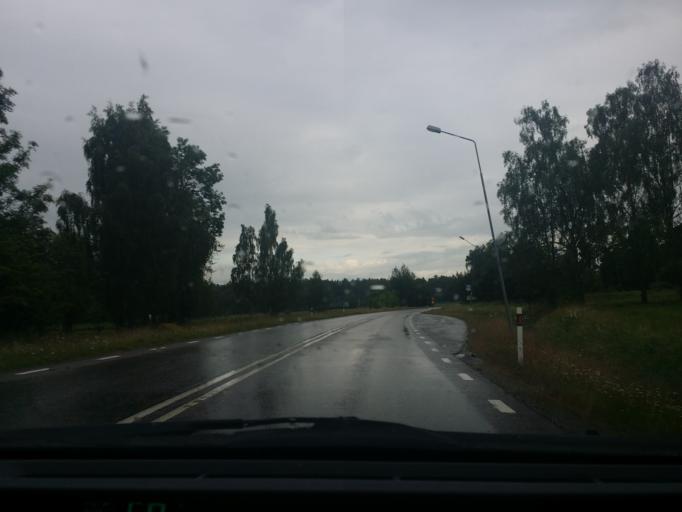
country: SE
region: OErebro
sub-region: Lindesbergs Kommun
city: Fellingsbro
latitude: 59.4449
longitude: 15.5955
